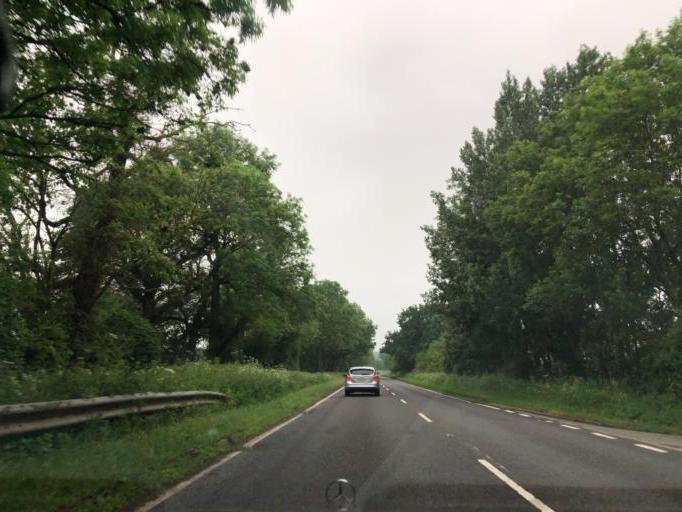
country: GB
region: England
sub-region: Warwickshire
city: Wellesbourne Mountford
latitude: 52.2251
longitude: -1.5276
